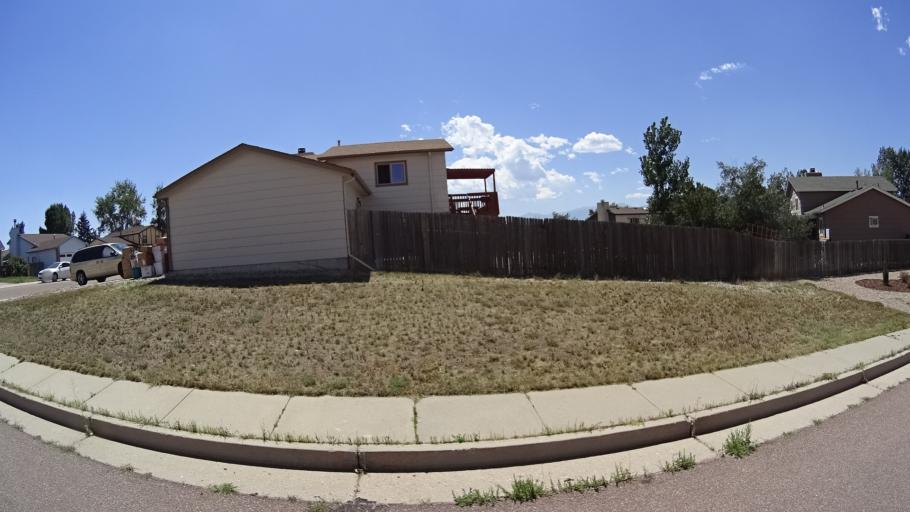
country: US
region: Colorado
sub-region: El Paso County
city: Black Forest
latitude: 38.9493
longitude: -104.7538
